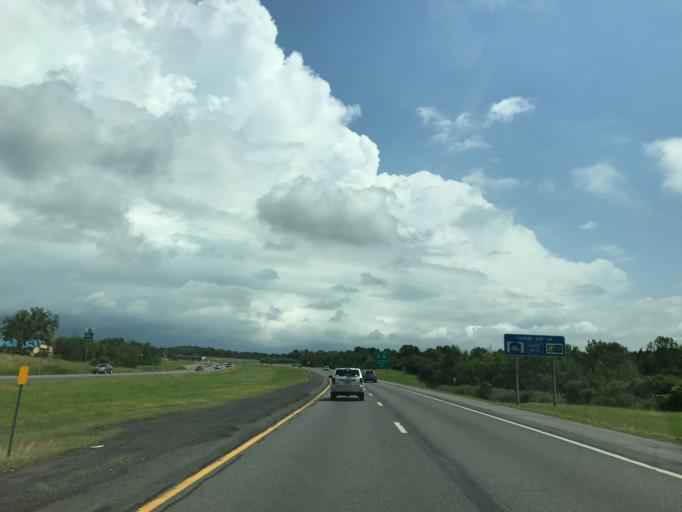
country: US
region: New York
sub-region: Greene County
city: Coxsackie
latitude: 42.3860
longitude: -73.8293
